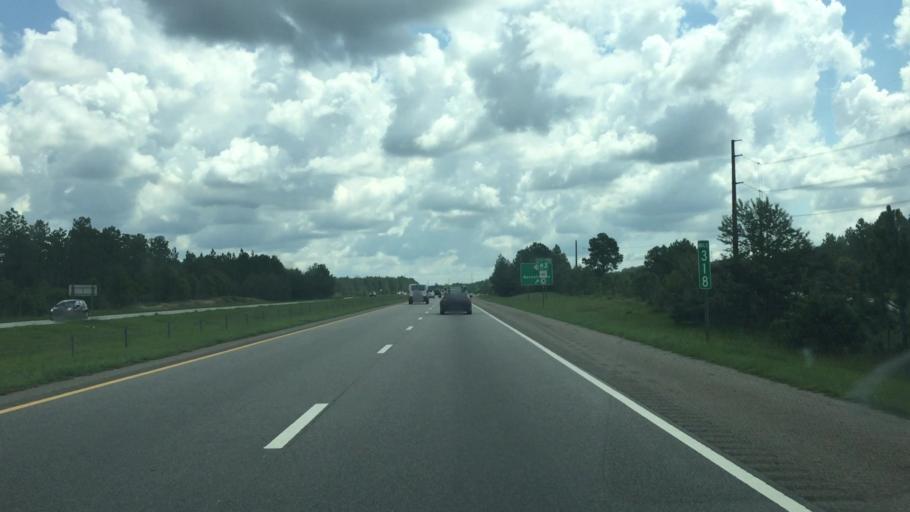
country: US
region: North Carolina
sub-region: Richmond County
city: Hamlet
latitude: 34.8550
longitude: -79.7029
